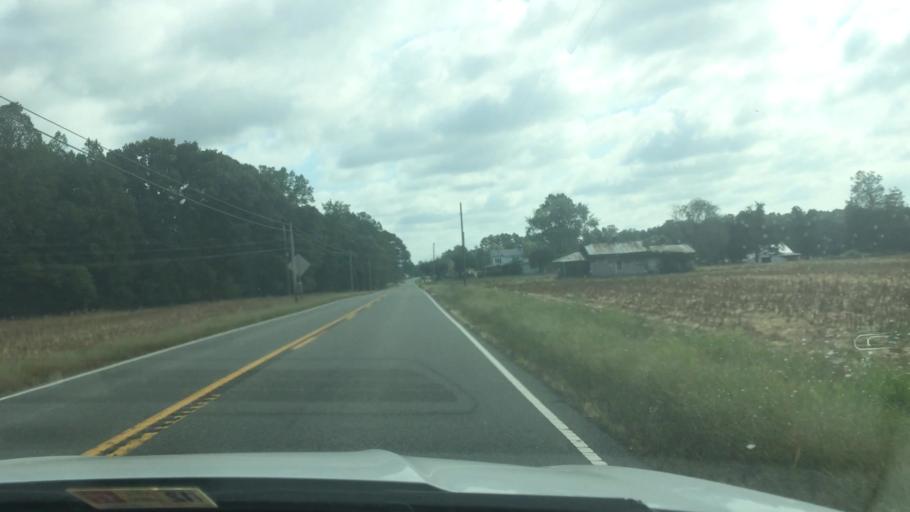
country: US
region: Virginia
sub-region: Northumberland County
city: Heathsville
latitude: 37.8458
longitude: -76.5808
